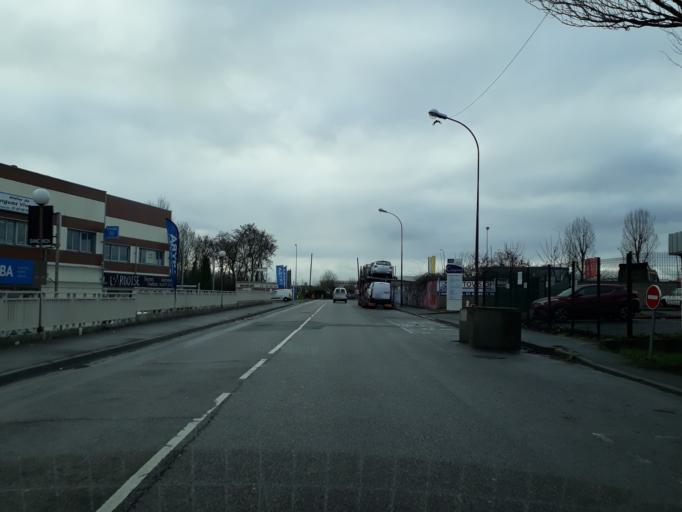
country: FR
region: Ile-de-France
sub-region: Departement de l'Essonne
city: Ormoy
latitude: 48.5696
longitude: 2.4513
